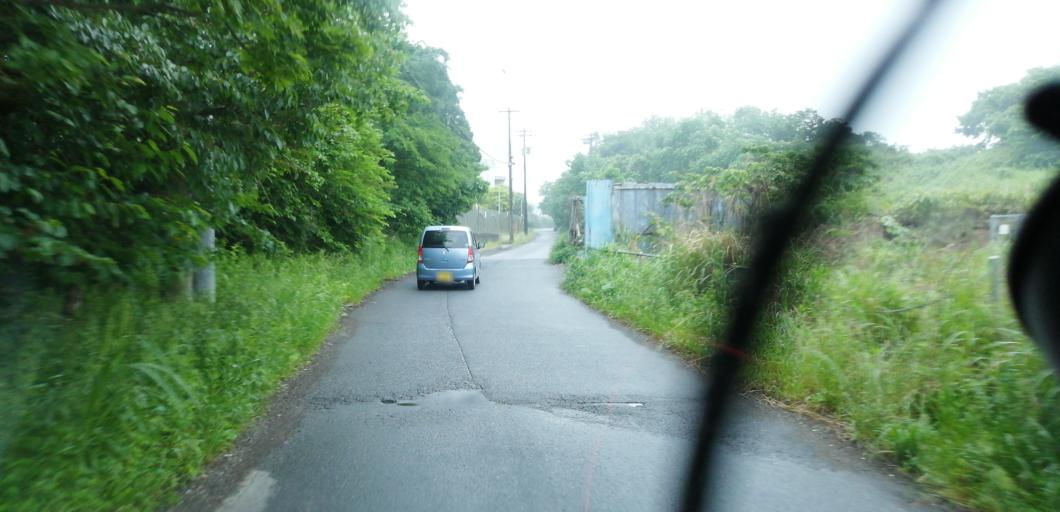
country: JP
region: Chiba
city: Ichihara
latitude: 35.4751
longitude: 140.1494
